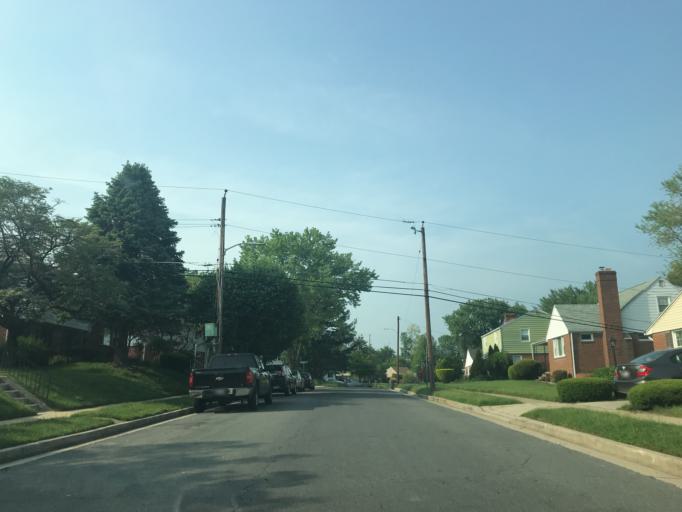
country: US
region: Maryland
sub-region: Baltimore County
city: Towson
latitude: 39.3804
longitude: -76.5768
